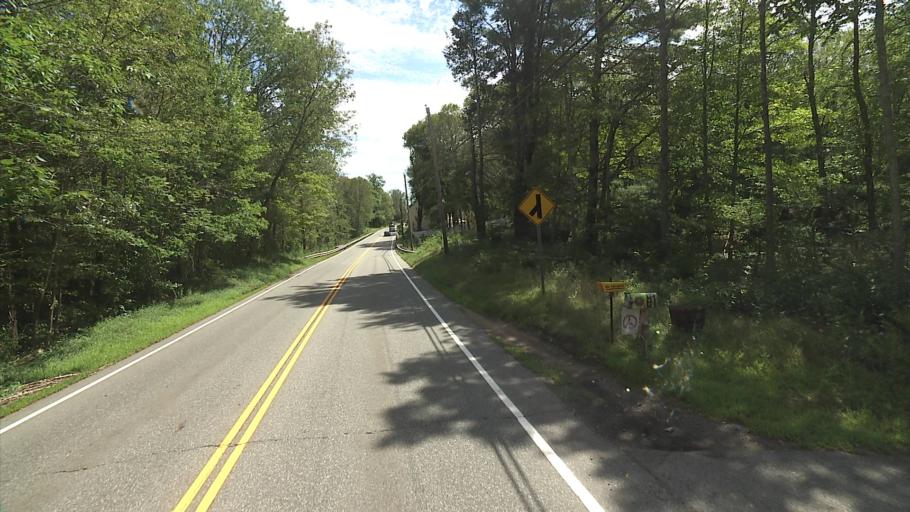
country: US
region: Connecticut
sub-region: Tolland County
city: Mansfield City
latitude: 41.7688
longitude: -72.2013
